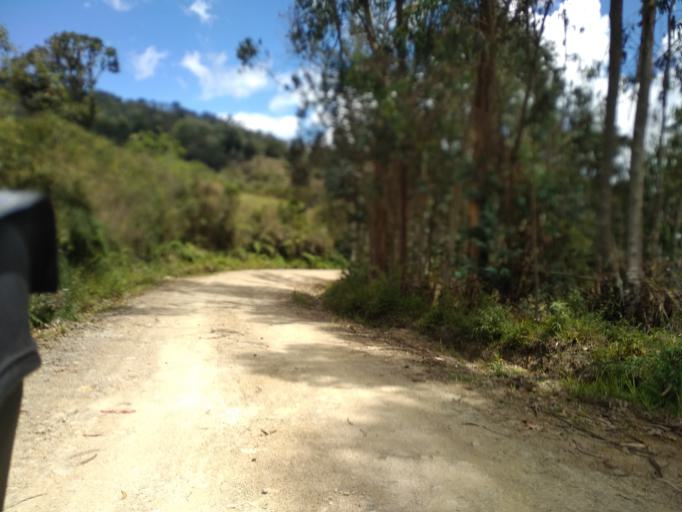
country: CO
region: Boyaca
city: Duitama
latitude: 5.9430
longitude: -73.1344
